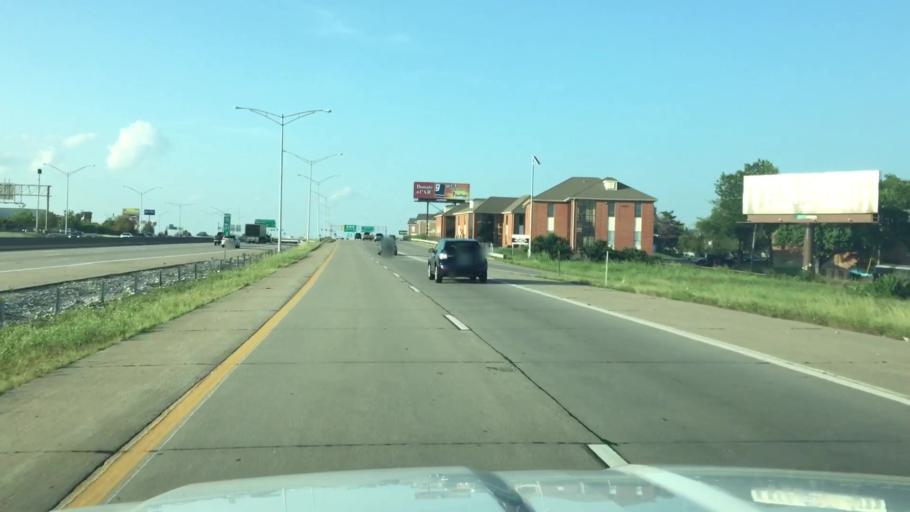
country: US
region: Missouri
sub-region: Saint Louis County
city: Mehlville
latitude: 38.5058
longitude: -90.3372
